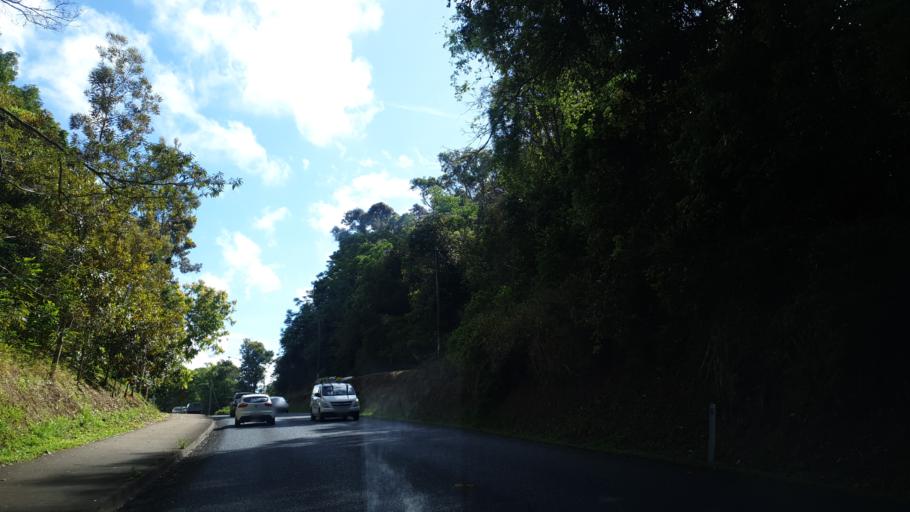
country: AU
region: Queensland
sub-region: Tablelands
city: Atherton
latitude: -17.3548
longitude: 145.5872
